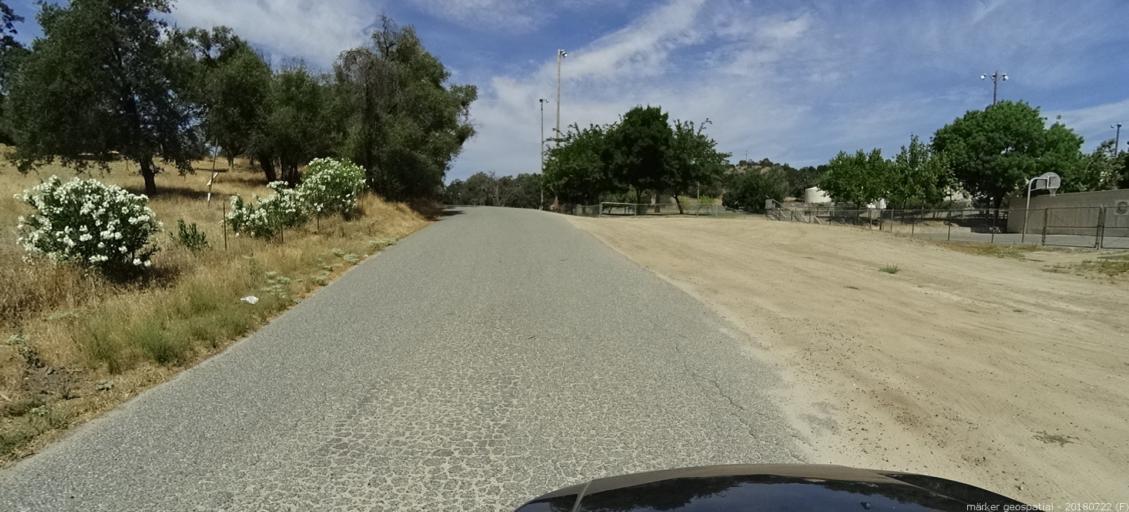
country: US
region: California
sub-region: Madera County
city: Coarsegold
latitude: 37.2537
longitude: -119.7179
